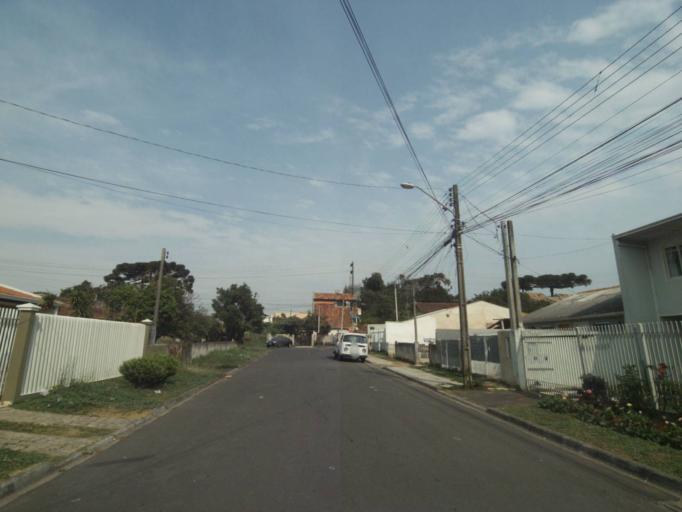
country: BR
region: Parana
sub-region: Pinhais
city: Pinhais
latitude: -25.4789
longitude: -49.2118
